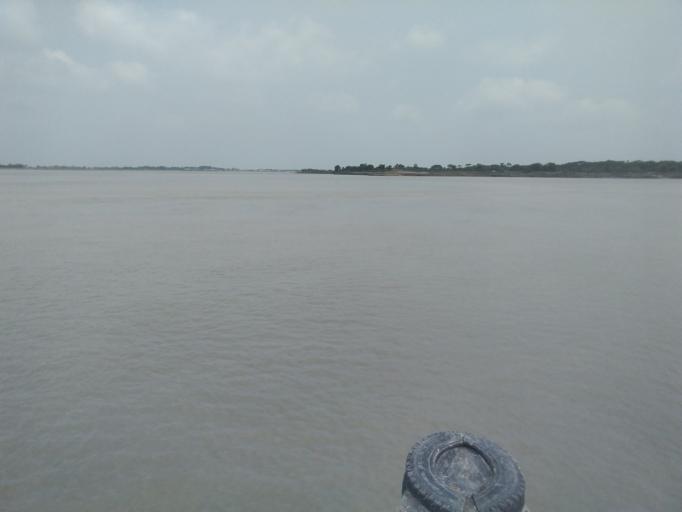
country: BD
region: Khulna
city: Phultala
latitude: 22.6428
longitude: 89.4130
